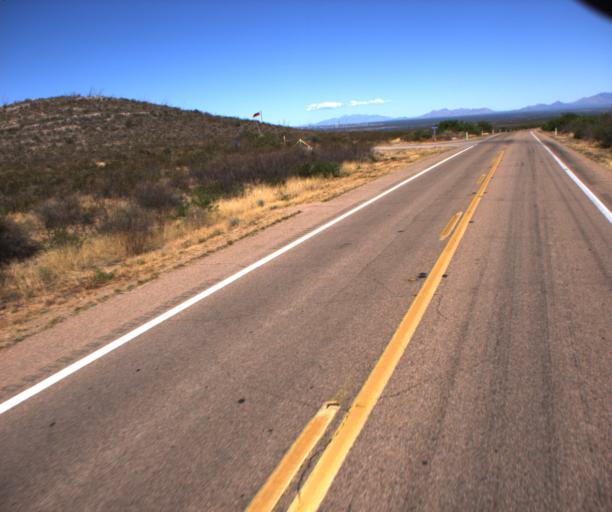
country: US
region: Arizona
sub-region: Cochise County
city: Bisbee
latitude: 31.5252
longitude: -110.0461
